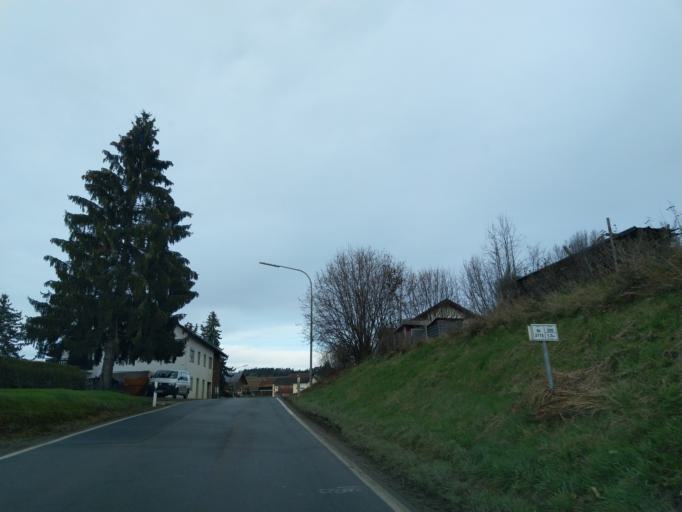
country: DE
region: Bavaria
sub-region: Lower Bavaria
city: Rossbach
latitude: 48.6343
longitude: 12.9657
